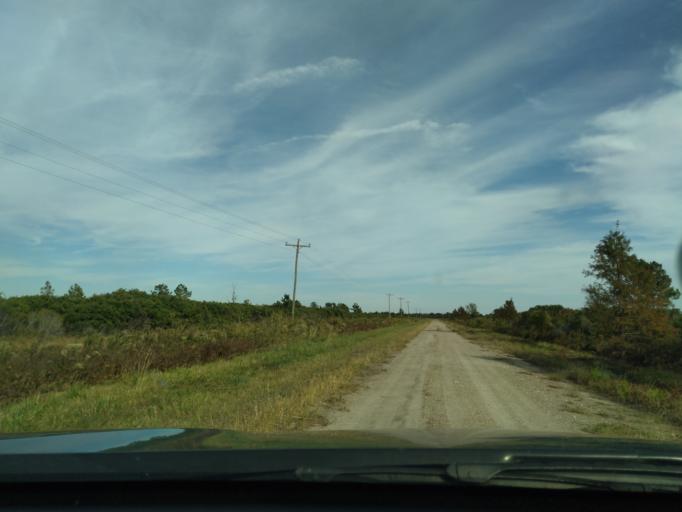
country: US
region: North Carolina
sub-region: Beaufort County
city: Belhaven
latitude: 35.6901
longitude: -76.5372
